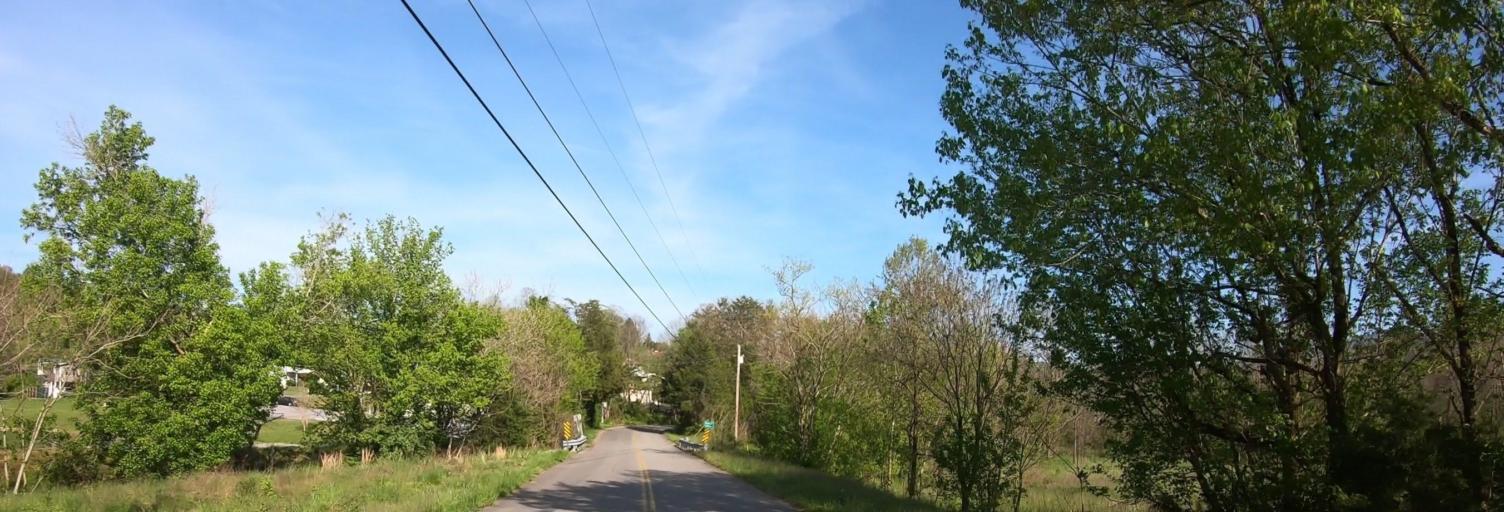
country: US
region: Tennessee
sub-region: Blount County
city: Wildwood
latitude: 35.6781
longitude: -83.7917
